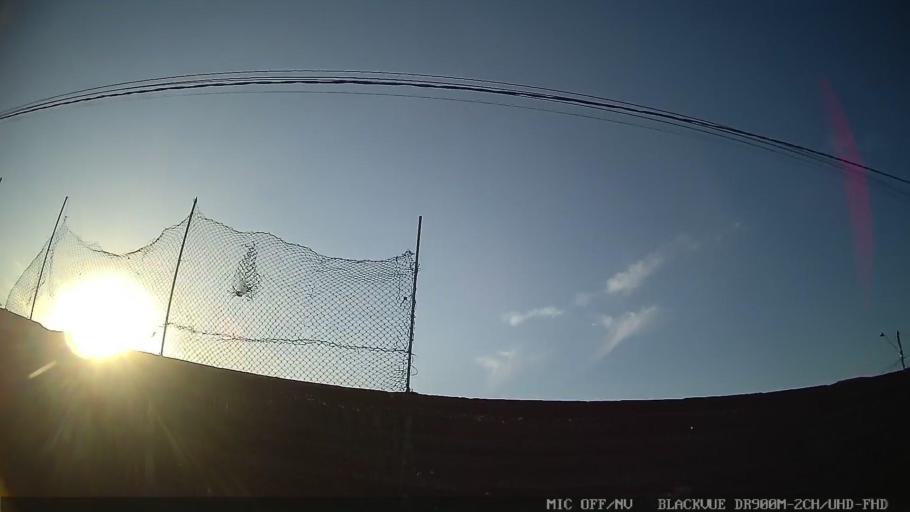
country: BR
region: Sao Paulo
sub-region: Guaruja
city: Guaruja
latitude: -23.9727
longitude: -46.2725
